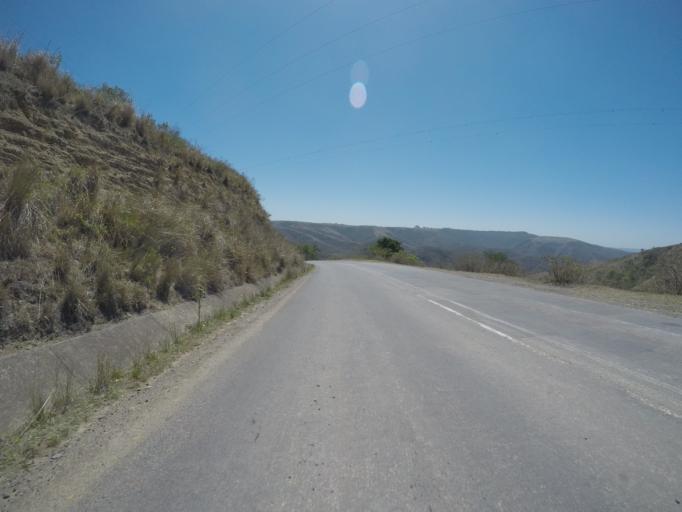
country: ZA
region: Eastern Cape
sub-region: OR Tambo District Municipality
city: Mthatha
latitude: -31.9178
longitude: 28.9666
